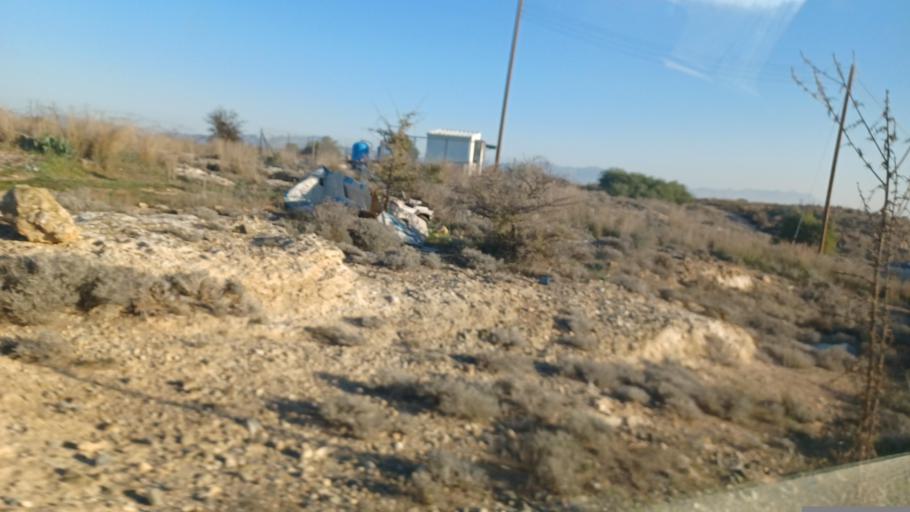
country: CY
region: Lefkosia
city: Kato Deftera
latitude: 35.1401
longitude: 33.2813
